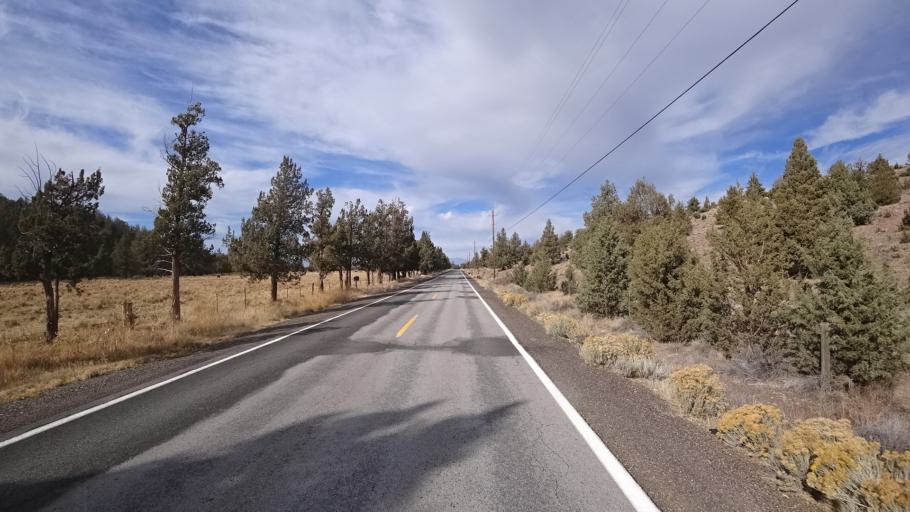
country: US
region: California
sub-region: Siskiyou County
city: Weed
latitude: 41.5769
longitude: -122.3958
